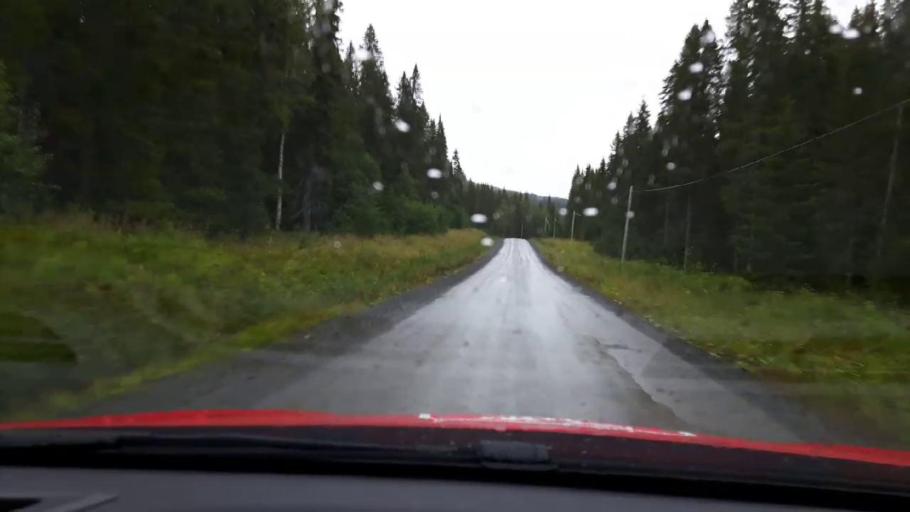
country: SE
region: Jaemtland
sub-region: Are Kommun
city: Are
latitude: 63.4858
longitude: 12.7815
